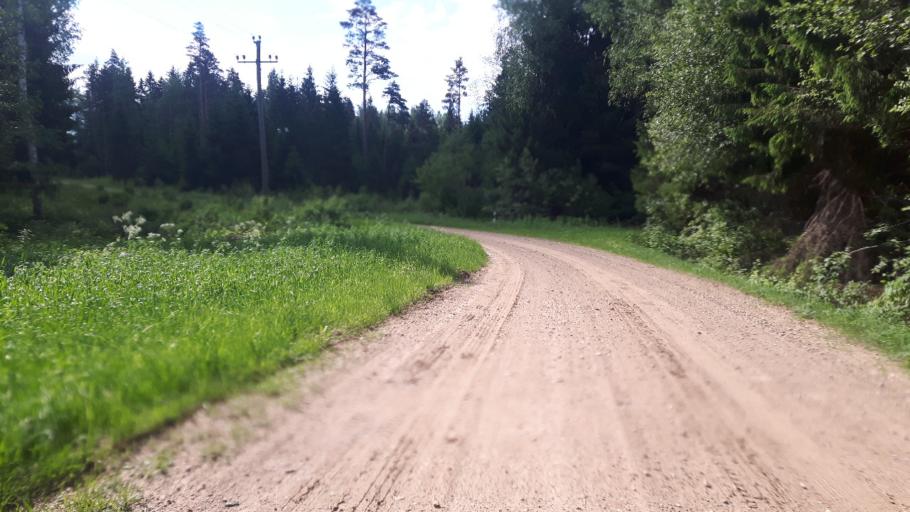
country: EE
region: Paernumaa
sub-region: Vaendra vald (alev)
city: Vandra
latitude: 58.7222
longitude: 25.0375
